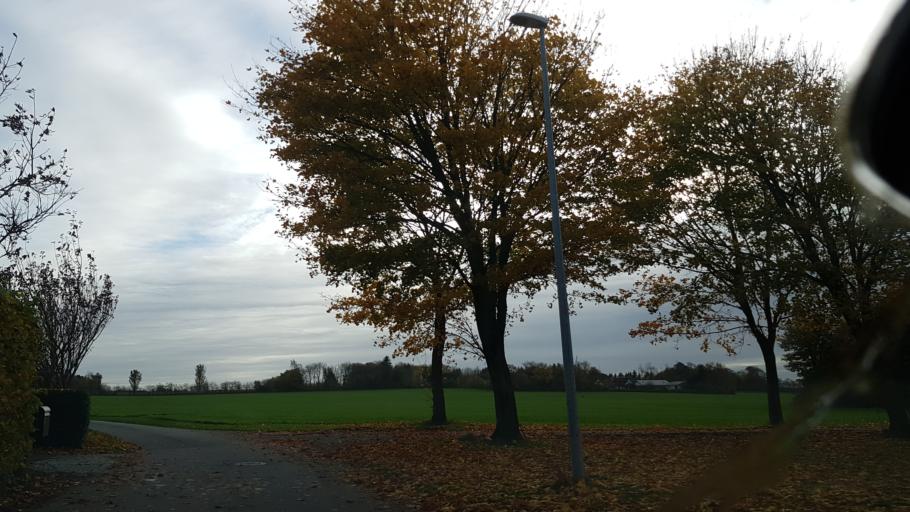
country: DK
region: South Denmark
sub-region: Haderslev Kommune
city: Gram
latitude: 55.2589
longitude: 9.1200
